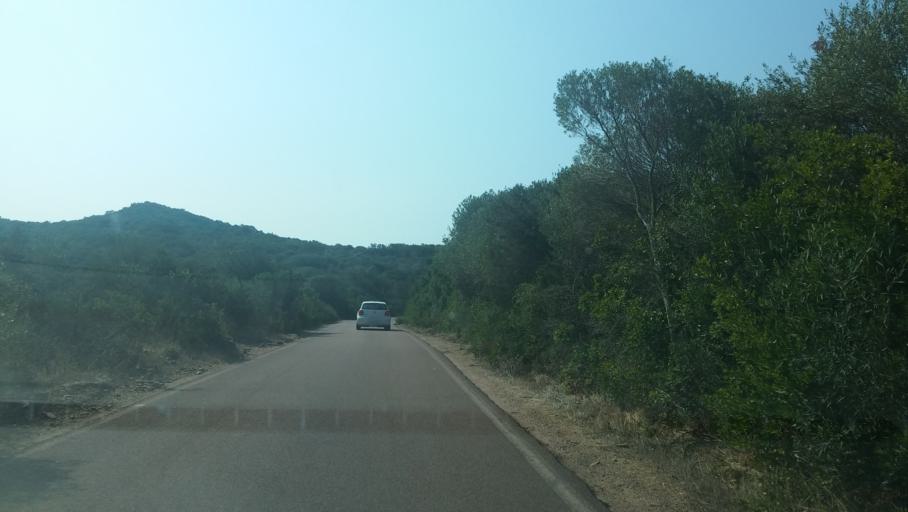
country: IT
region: Sardinia
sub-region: Provincia di Olbia-Tempio
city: La Maddalena
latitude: 41.1953
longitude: 9.4577
